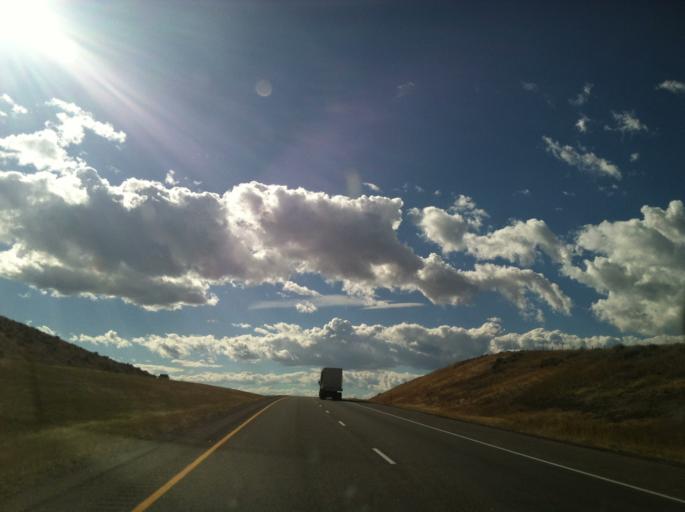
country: US
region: Montana
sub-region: Gallatin County
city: Three Forks
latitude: 45.9195
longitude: -111.6672
